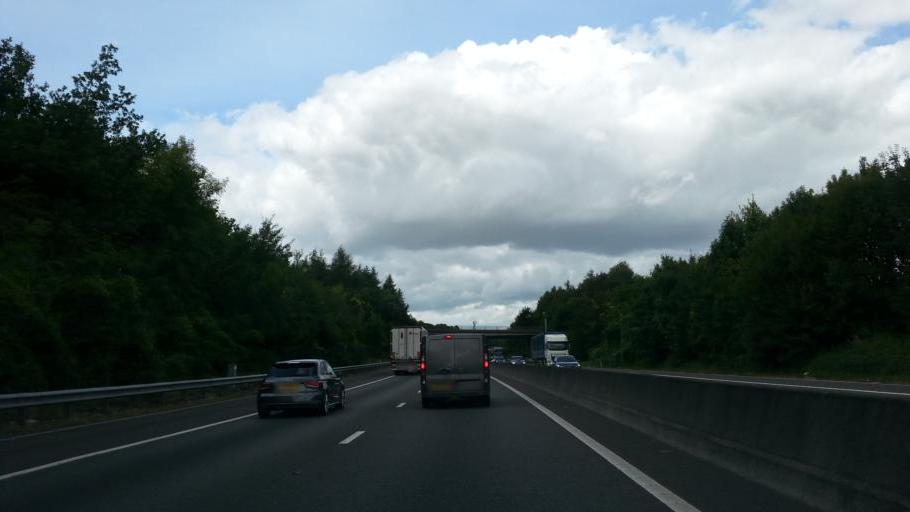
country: GB
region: England
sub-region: Essex
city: Elsenham
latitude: 51.9093
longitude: 0.2219
